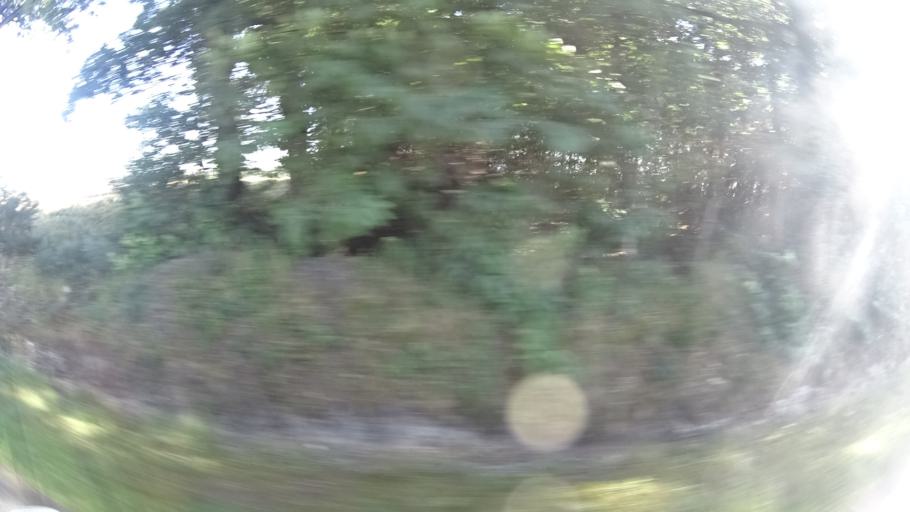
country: FR
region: Brittany
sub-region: Departement d'Ille-et-Vilaine
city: Langon
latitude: 47.7407
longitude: -1.8049
